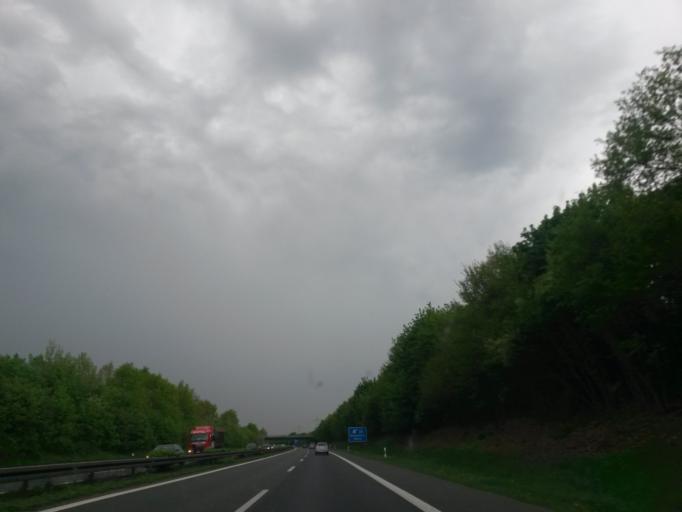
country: DE
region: Bavaria
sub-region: Upper Franconia
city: Altendorf
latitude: 49.8040
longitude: 11.0165
